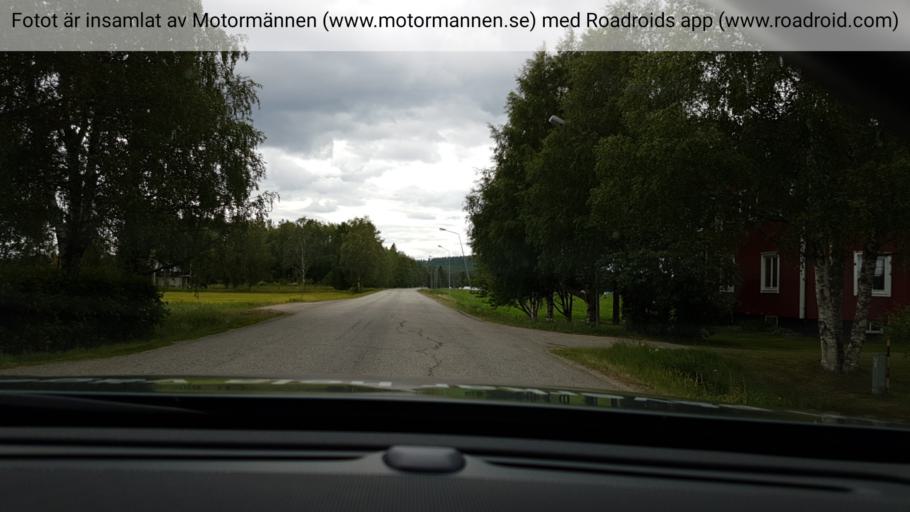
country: SE
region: Vaesterbotten
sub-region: Vindelns Kommun
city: Vindeln
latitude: 64.0878
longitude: 19.6470
